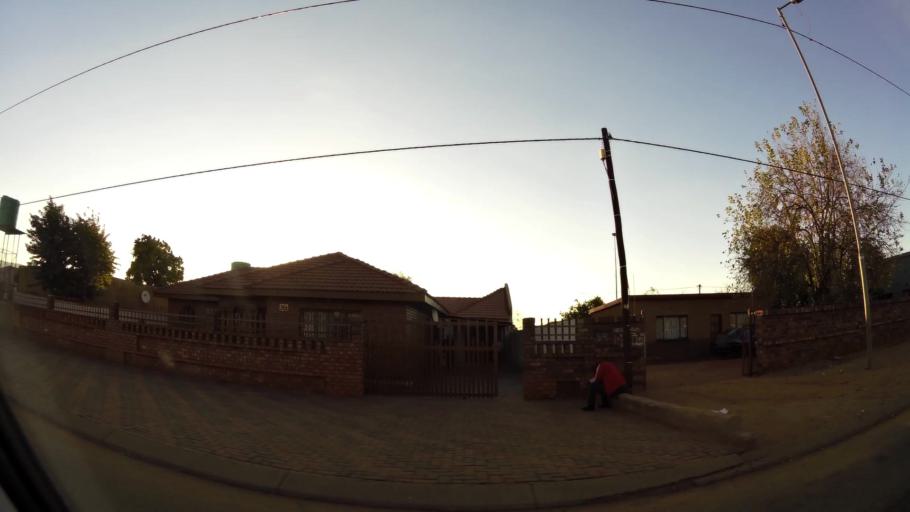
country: ZA
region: Limpopo
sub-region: Waterberg District Municipality
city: Mokopane
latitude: -24.1405
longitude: 28.9960
